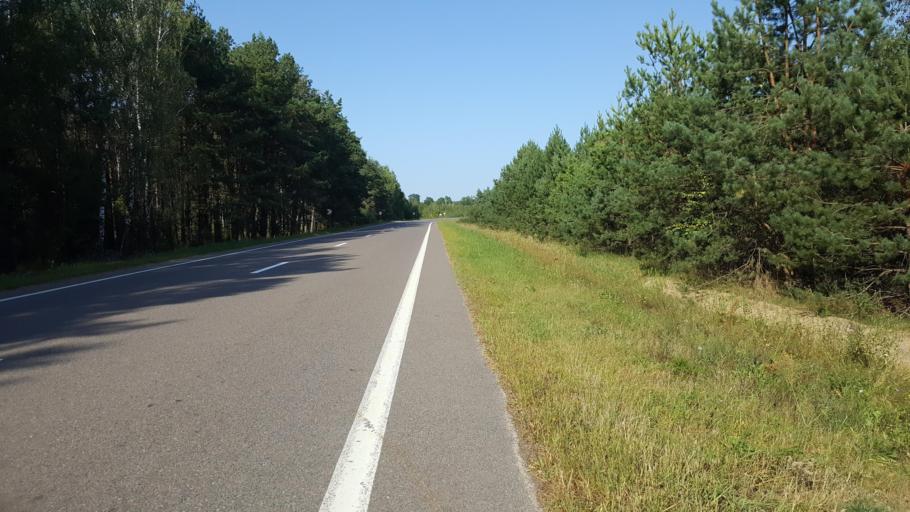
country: PL
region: Podlasie
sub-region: Powiat hajnowski
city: Hajnowka
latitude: 52.5611
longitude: 23.6056
